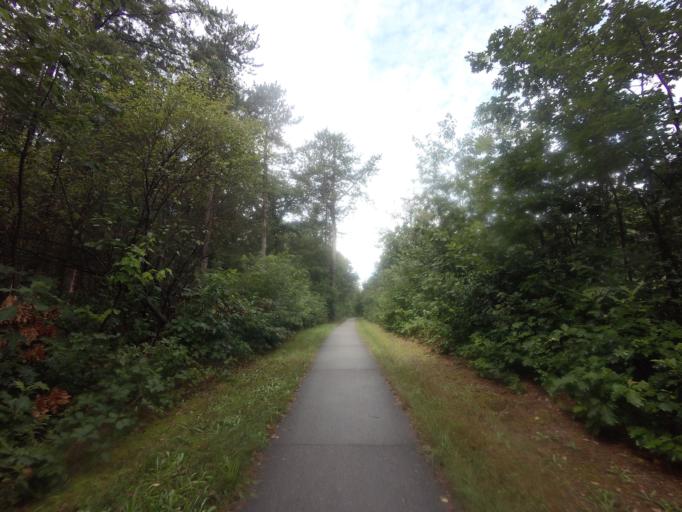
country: NL
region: Overijssel
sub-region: Gemeente Staphorst
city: Staphorst
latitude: 52.6213
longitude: 6.3026
